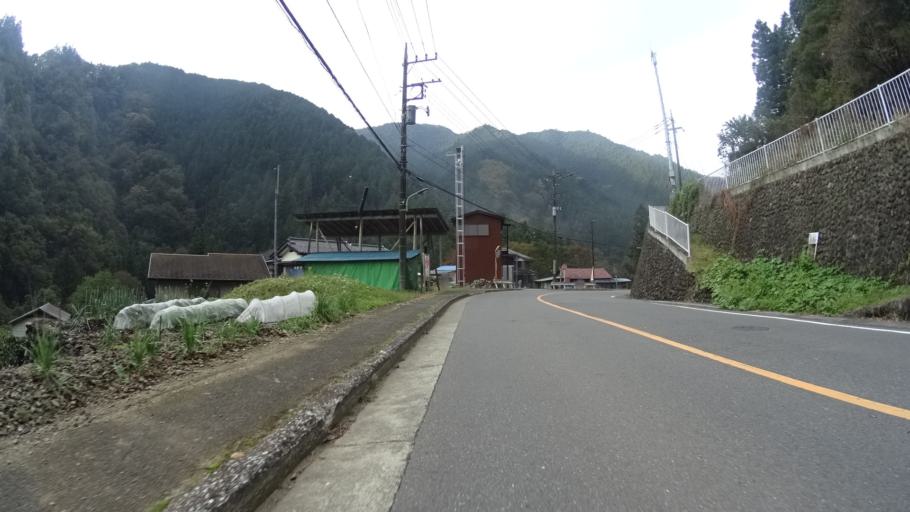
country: JP
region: Tokyo
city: Itsukaichi
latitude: 35.7031
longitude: 139.1420
